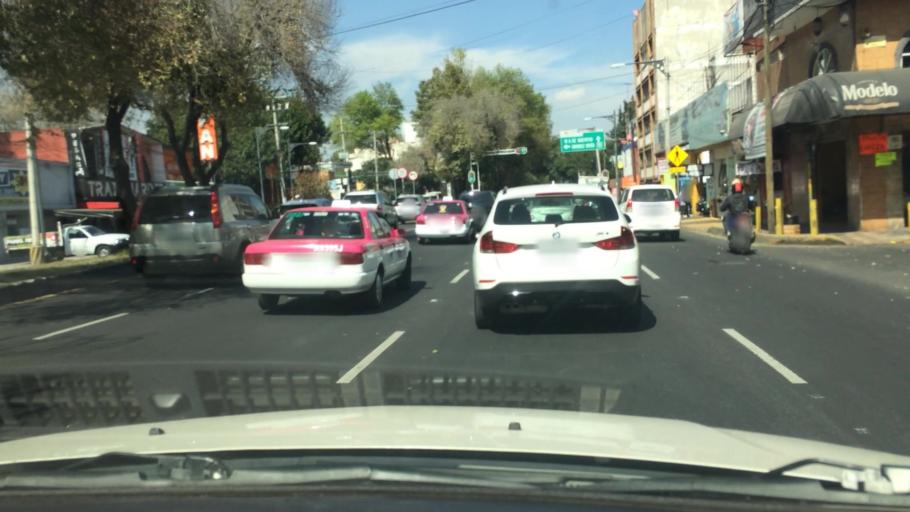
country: MX
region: Mexico City
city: Coyoacan
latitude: 19.3392
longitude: -99.1478
